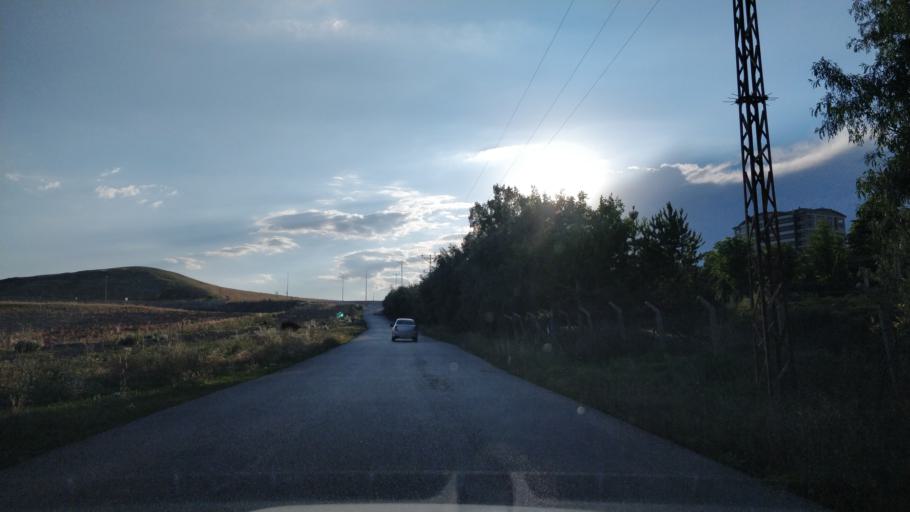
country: TR
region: Ankara
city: Etimesgut
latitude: 39.8271
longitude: 32.5590
